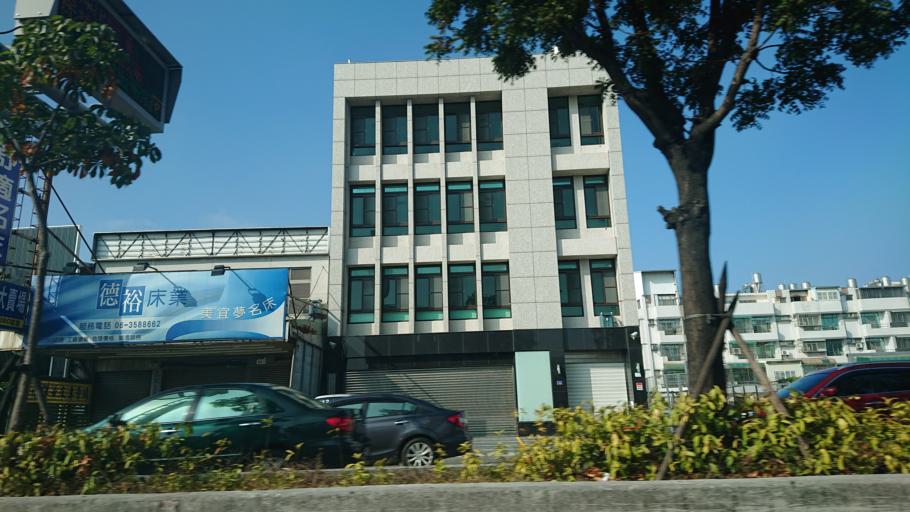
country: TW
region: Taiwan
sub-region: Tainan
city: Tainan
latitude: 23.0082
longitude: 120.1859
